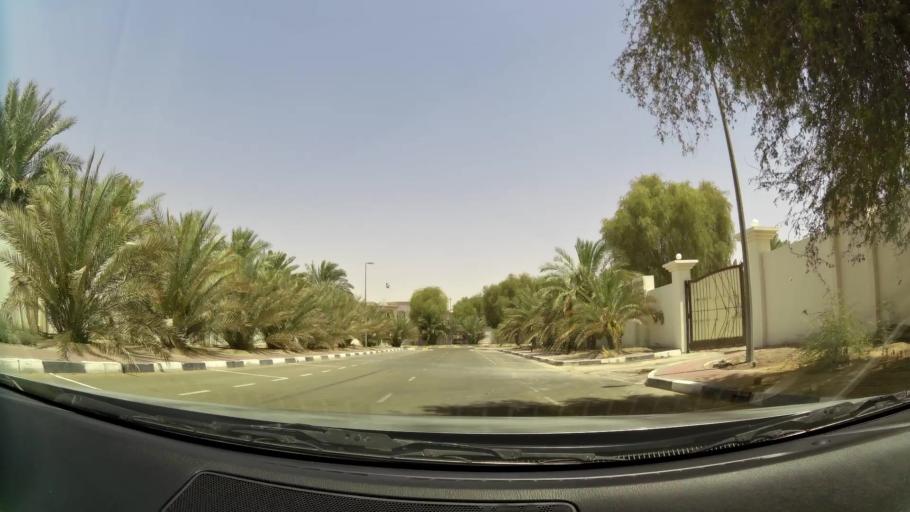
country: OM
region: Al Buraimi
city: Al Buraymi
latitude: 24.2796
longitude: 55.7558
